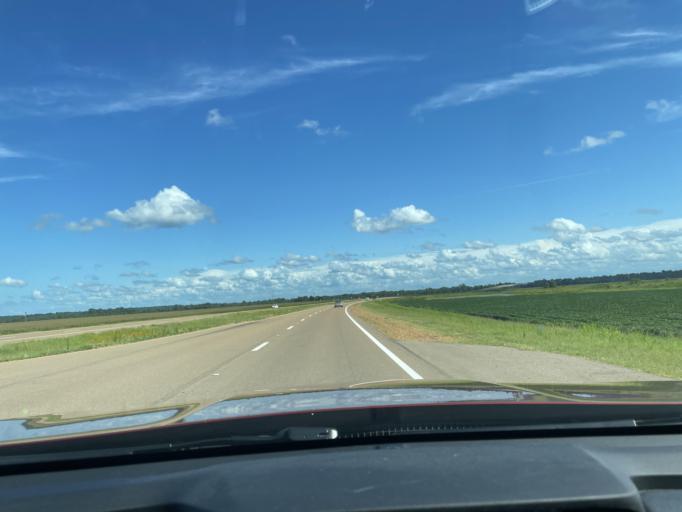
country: US
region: Mississippi
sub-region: Yazoo County
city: Yazoo City
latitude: 32.9467
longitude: -90.4173
